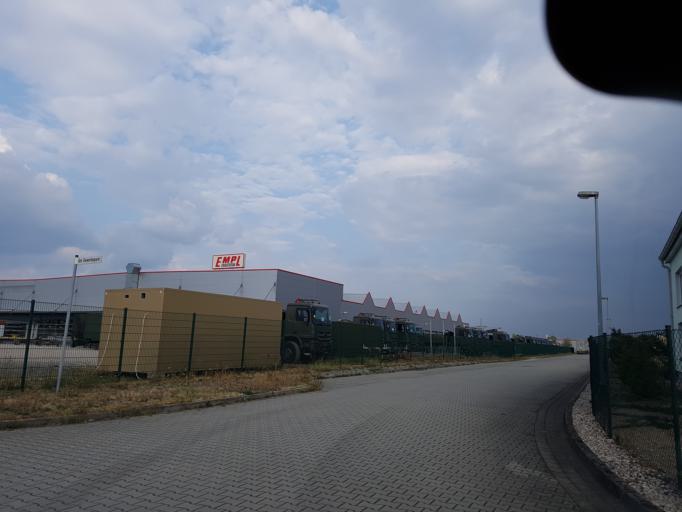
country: DE
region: Saxony-Anhalt
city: Elster
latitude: 51.8328
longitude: 12.8045
